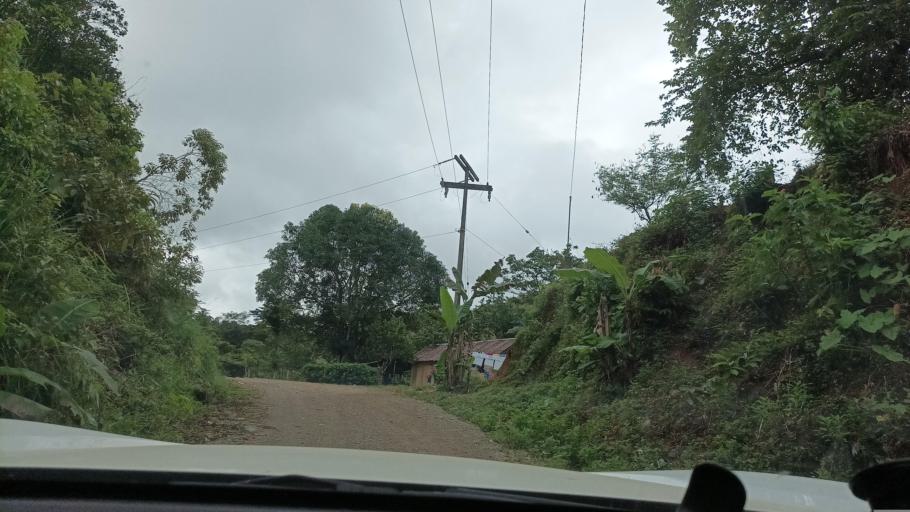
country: MX
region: Veracruz
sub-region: Uxpanapa
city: Poblado 10
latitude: 17.4268
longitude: -94.4206
